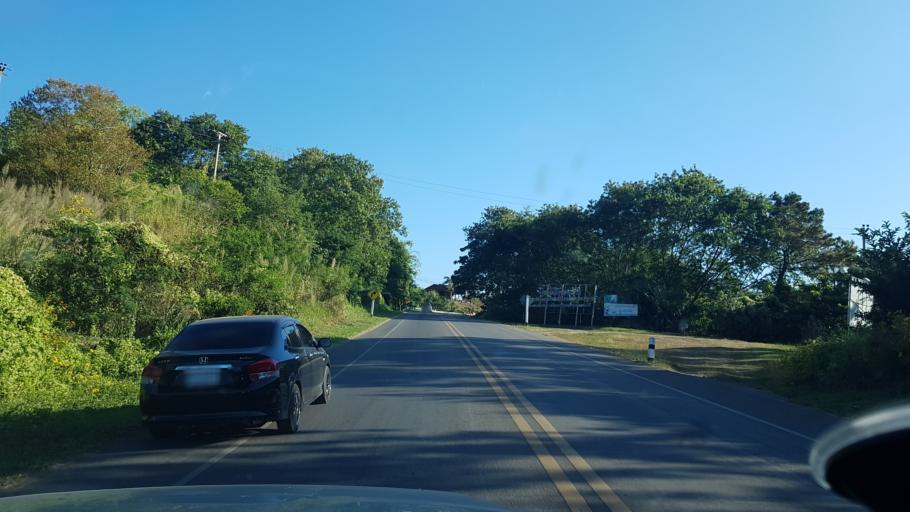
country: TH
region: Phetchabun
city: Khao Kho
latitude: 16.6703
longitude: 101.0258
